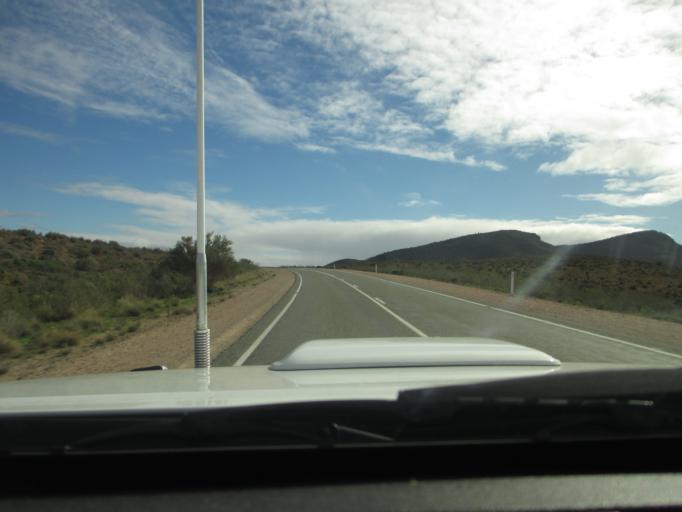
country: AU
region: South Australia
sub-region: Flinders Ranges
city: Quorn
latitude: -31.7986
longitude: 138.3601
